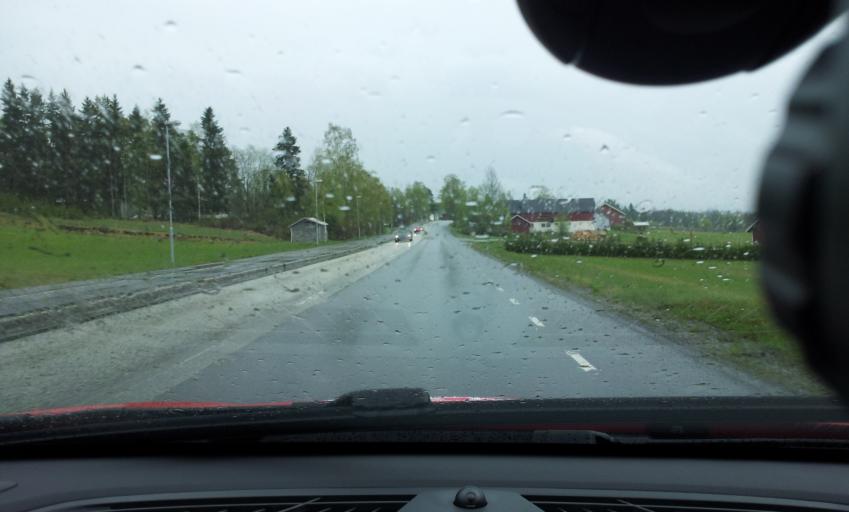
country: SE
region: Jaemtland
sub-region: OEstersunds Kommun
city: Brunflo
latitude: 63.1180
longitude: 14.7849
